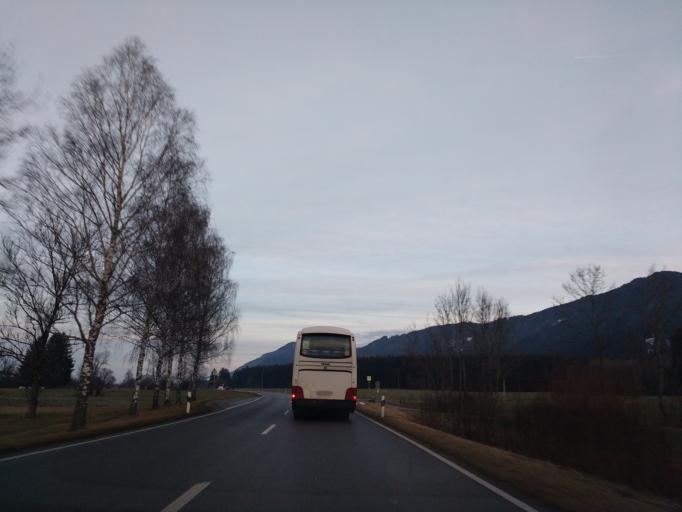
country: DE
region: Bavaria
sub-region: Swabia
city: Schwangau
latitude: 47.5854
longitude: 10.7620
